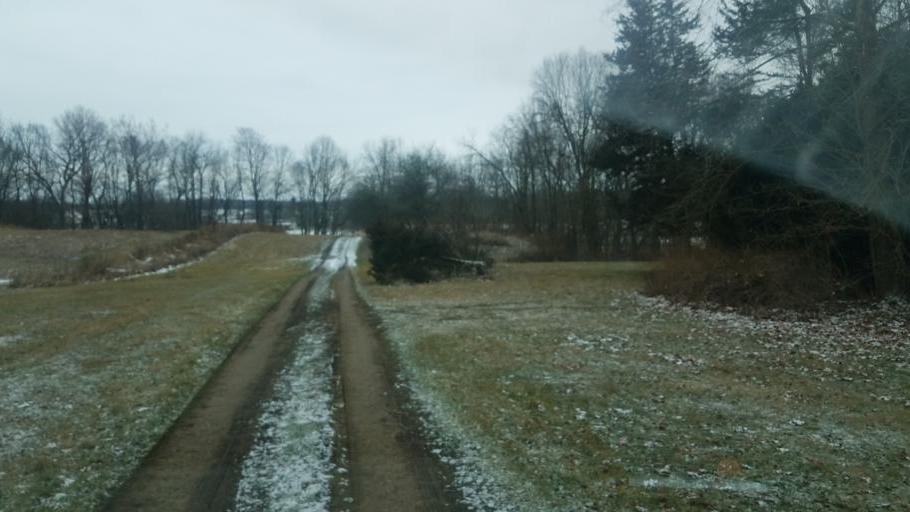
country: US
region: Ohio
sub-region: Knox County
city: Fredericktown
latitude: 40.4659
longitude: -82.6373
